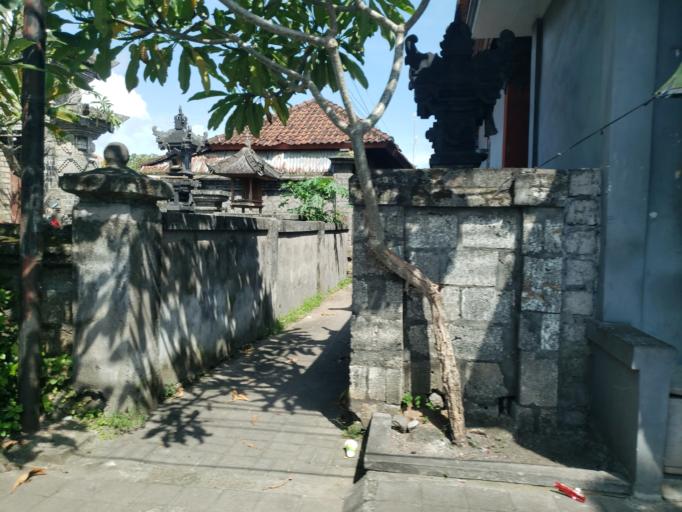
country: ID
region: Bali
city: Kangin
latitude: -8.8327
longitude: 115.1264
